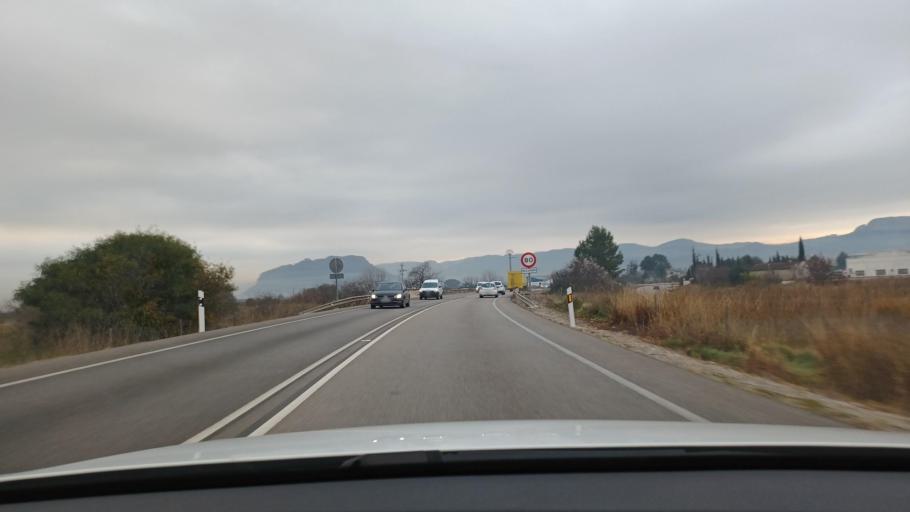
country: ES
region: Valencia
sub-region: Provincia de Valencia
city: Llosa de Ranes
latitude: 39.0137
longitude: -0.5367
